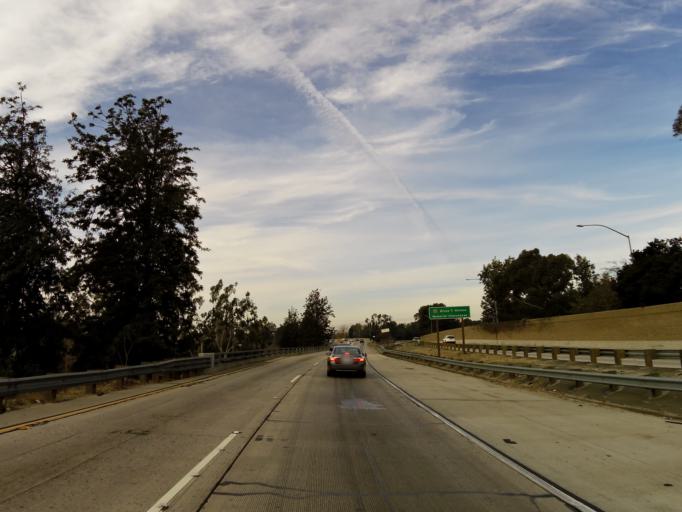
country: US
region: California
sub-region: Los Angeles County
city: North Hollywood
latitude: 34.1533
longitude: -118.3746
